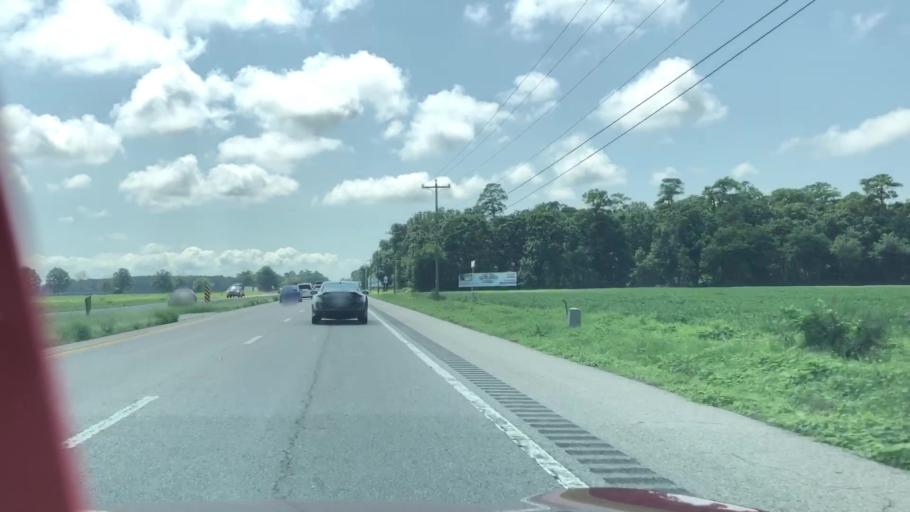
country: US
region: Virginia
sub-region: Northampton County
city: Cape Charles
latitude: 37.2446
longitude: -75.9719
